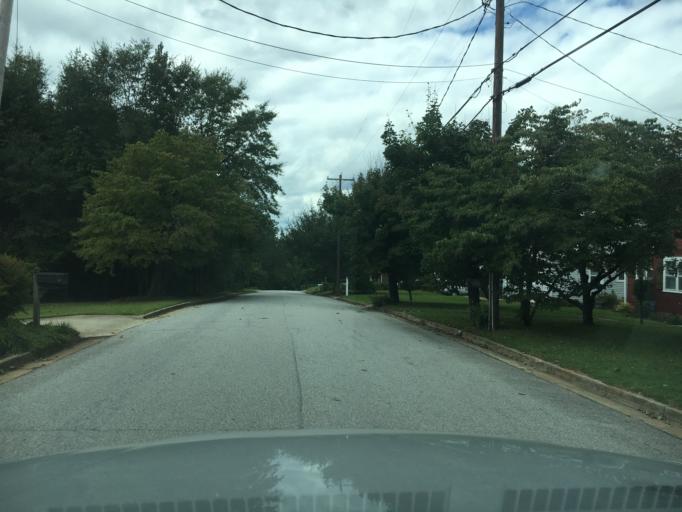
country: US
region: South Carolina
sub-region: Greenville County
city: Greer
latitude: 34.9505
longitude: -82.2266
